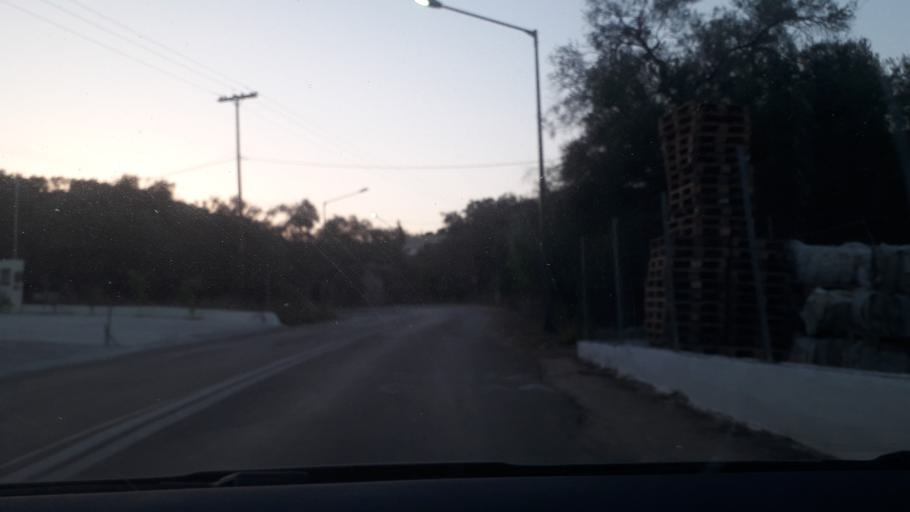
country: GR
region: Ionian Islands
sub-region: Nomos Kerkyras
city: Perivoli
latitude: 39.4424
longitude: 19.9543
